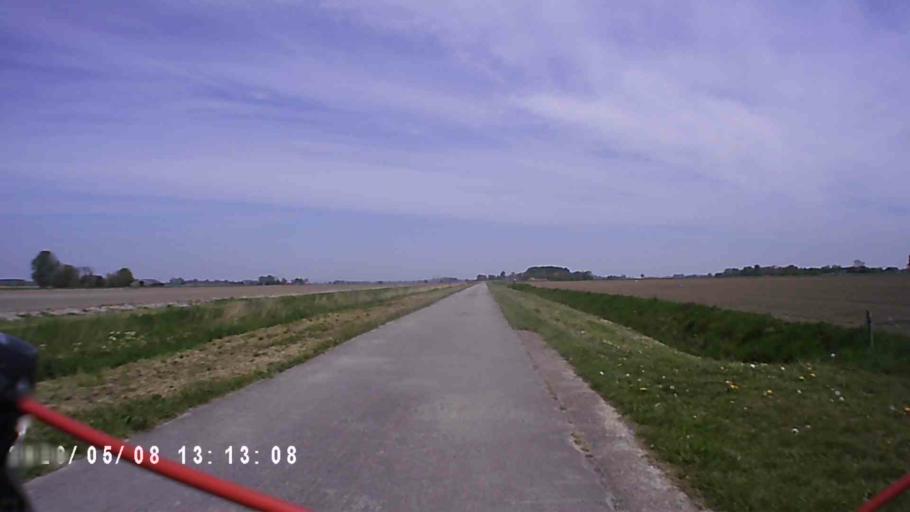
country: NL
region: Groningen
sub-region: Gemeente Bedum
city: Bedum
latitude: 53.2984
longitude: 6.6911
